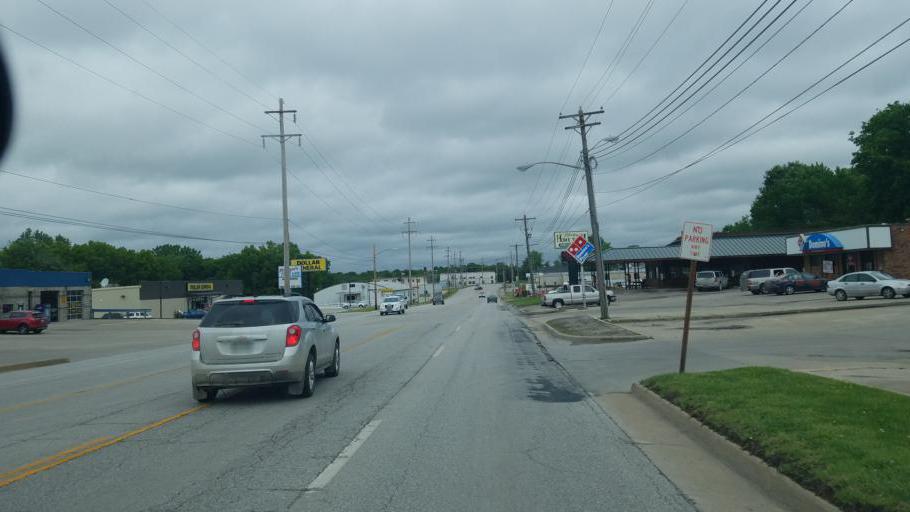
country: US
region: Missouri
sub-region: Livingston County
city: Chillicothe
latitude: 39.7996
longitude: -93.5537
